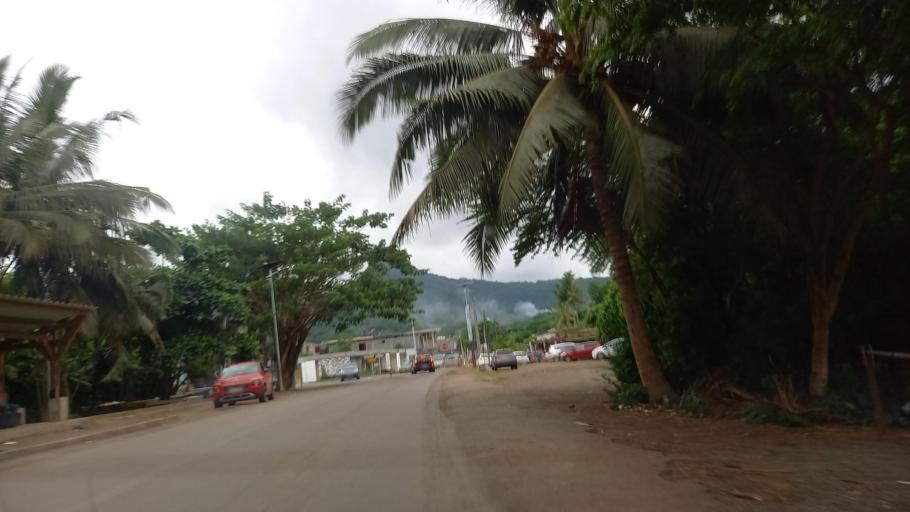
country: YT
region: Chirongui
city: Chirongui
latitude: -12.9324
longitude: 45.1520
